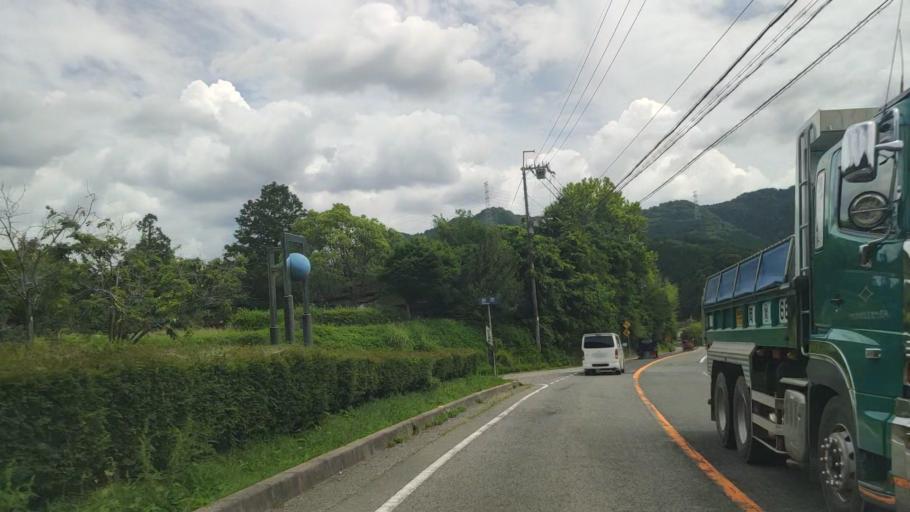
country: JP
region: Hyogo
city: Yamazakicho-nakabirose
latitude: 34.9860
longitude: 134.4133
